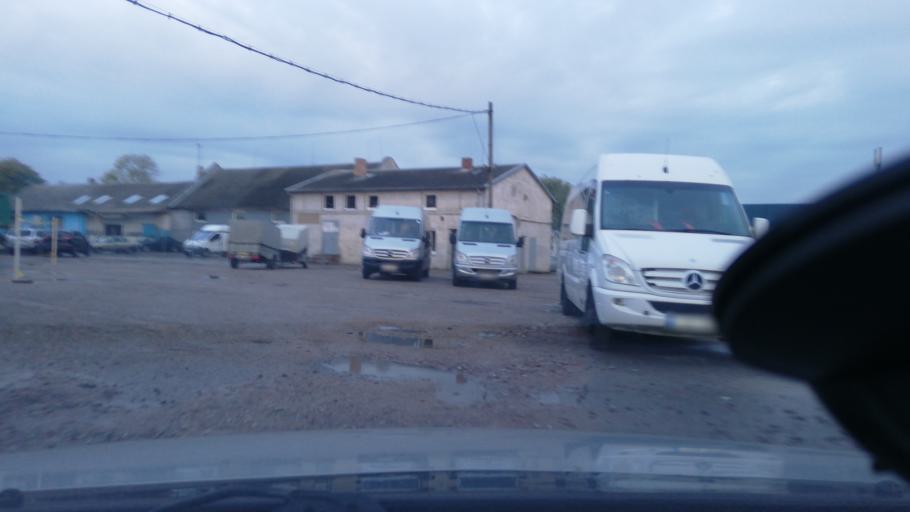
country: LT
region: Klaipedos apskritis
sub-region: Klaipeda
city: Klaipeda
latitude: 55.6876
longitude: 21.1849
